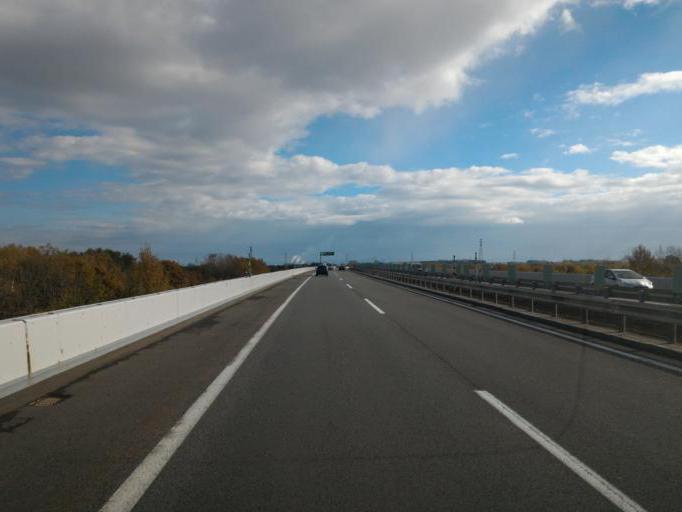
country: JP
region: Hokkaido
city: Ebetsu
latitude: 43.0924
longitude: 141.4673
